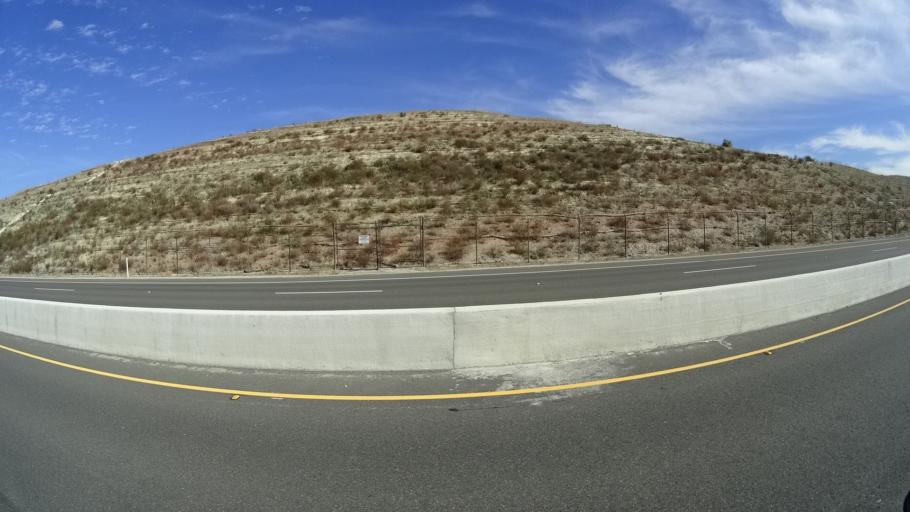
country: US
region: California
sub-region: Orange County
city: Ladera Ranch
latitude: 33.5586
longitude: -117.6025
